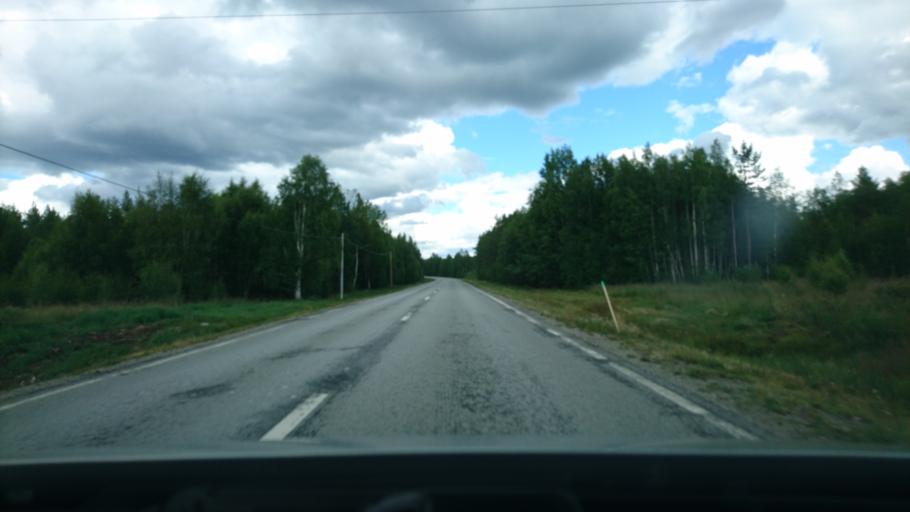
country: SE
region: Vaesterbotten
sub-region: Asele Kommun
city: Asele
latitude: 63.8716
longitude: 17.1919
